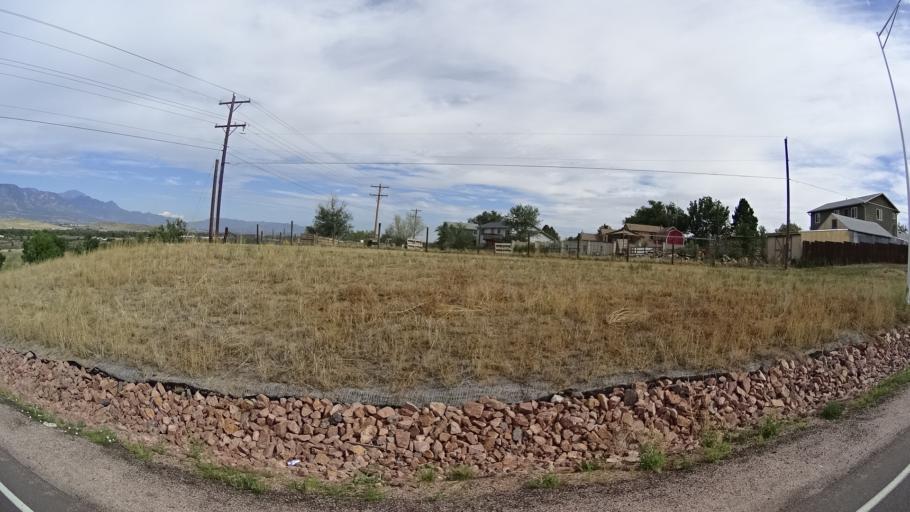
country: US
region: Colorado
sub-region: El Paso County
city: Fountain
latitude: 38.7081
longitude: -104.7028
